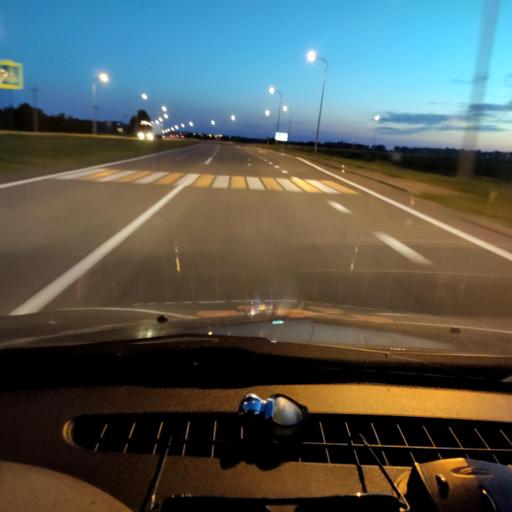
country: RU
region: Belgorod
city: Razumnoye
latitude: 50.7216
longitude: 36.8137
